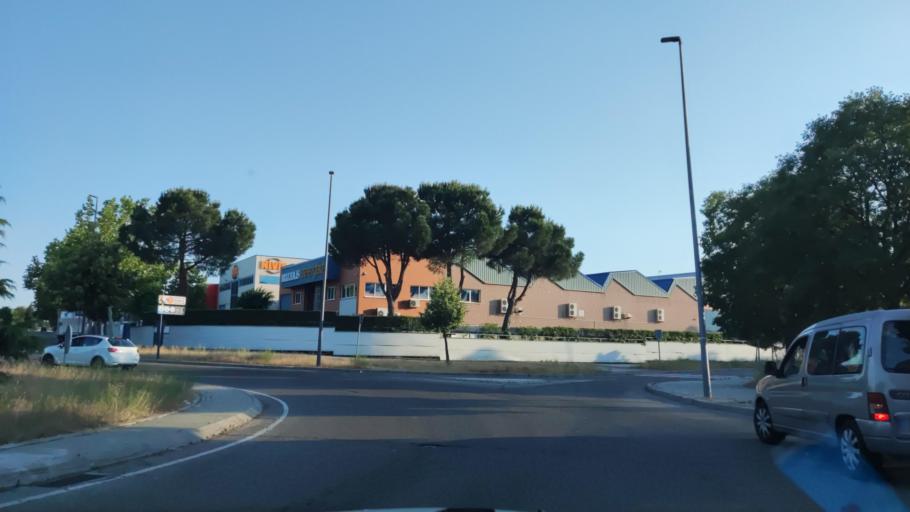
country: ES
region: Madrid
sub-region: Provincia de Madrid
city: Pinto
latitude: 40.2681
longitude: -3.6948
